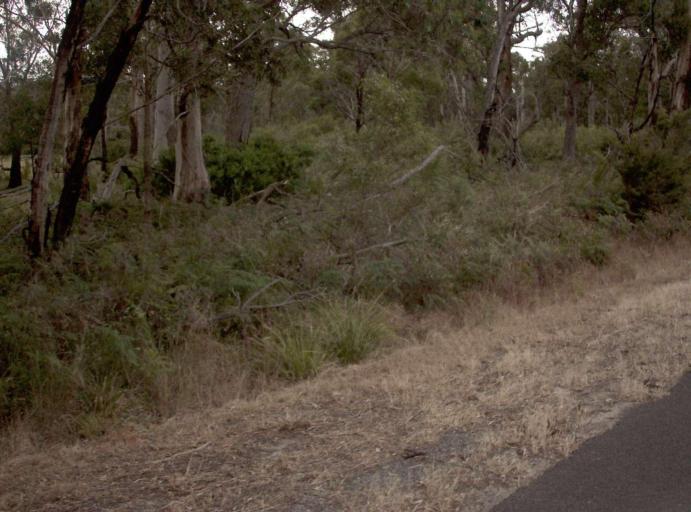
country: AU
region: Victoria
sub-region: Wellington
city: Sale
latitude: -38.4662
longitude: 146.9317
